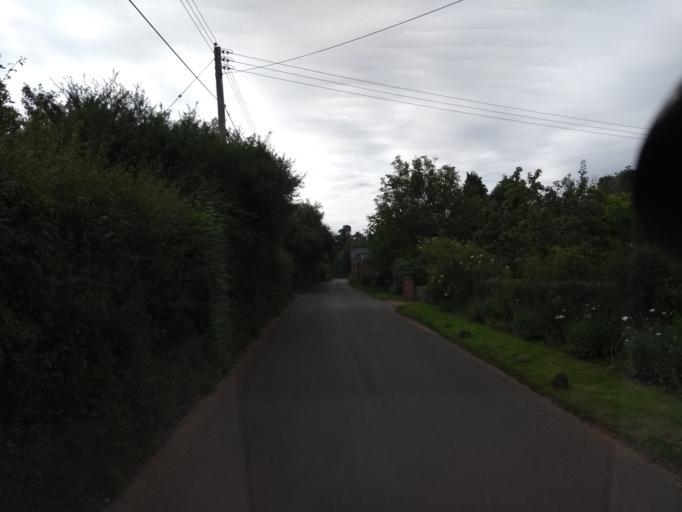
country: GB
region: England
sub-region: Somerset
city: Williton
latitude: 51.1385
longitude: -3.3395
